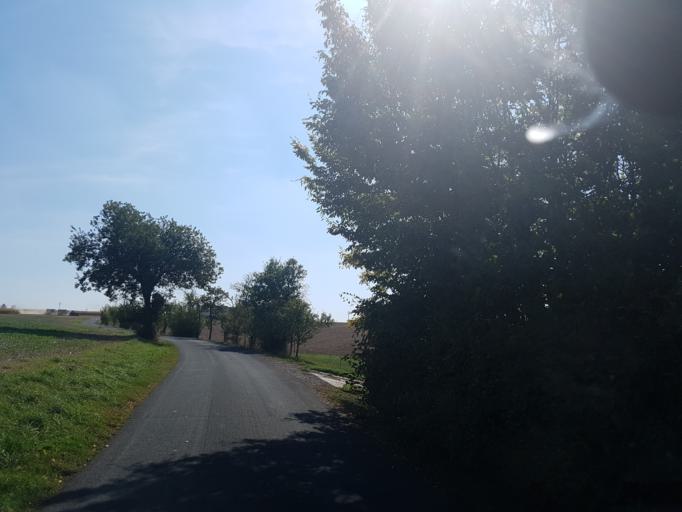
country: DE
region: Saxony
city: Kriebstein
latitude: 51.0411
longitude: 12.9862
